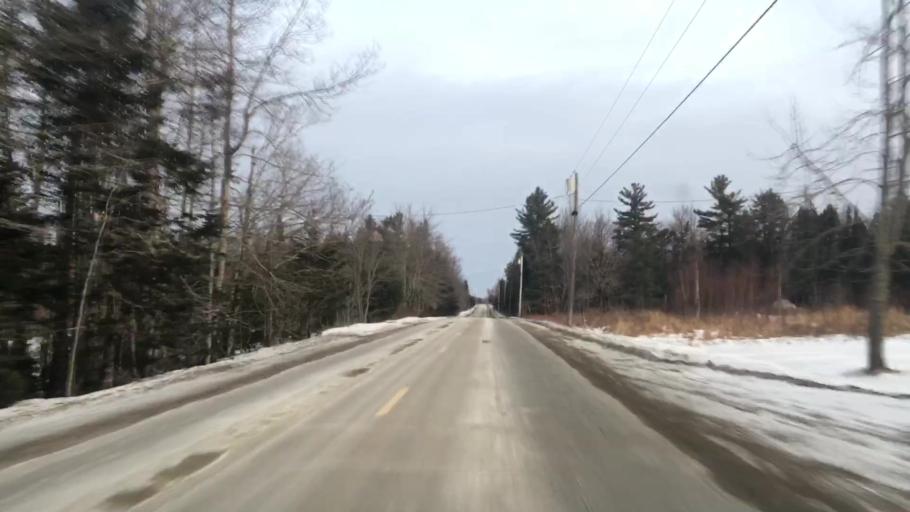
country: US
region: Maine
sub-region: Hancock County
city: Franklin
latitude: 44.7266
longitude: -68.3348
